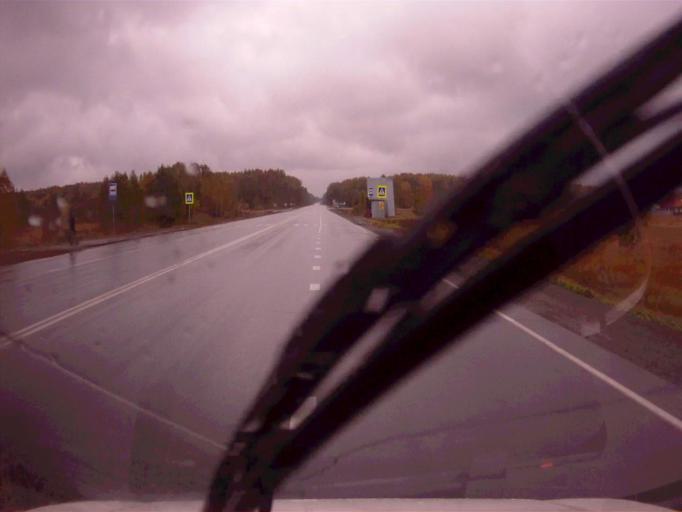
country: RU
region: Chelyabinsk
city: Argayash
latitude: 55.4564
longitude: 60.9272
